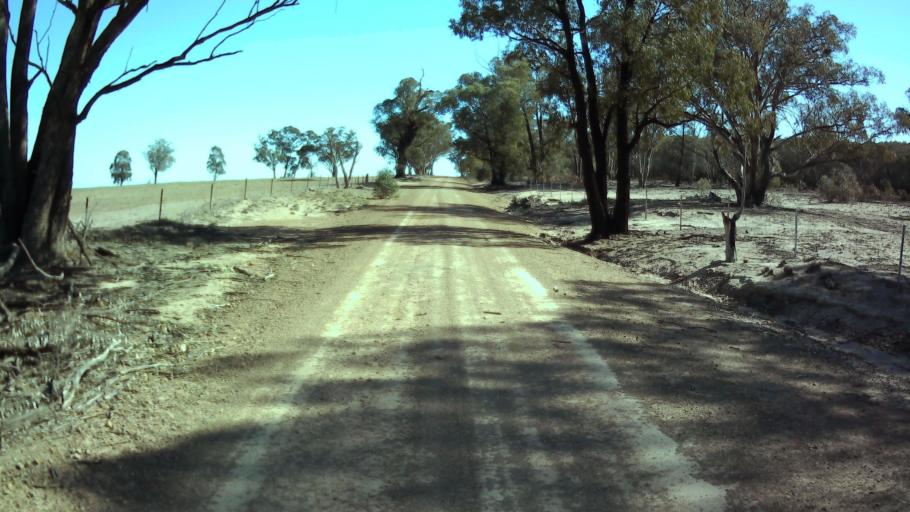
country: AU
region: New South Wales
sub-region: Weddin
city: Grenfell
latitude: -33.7563
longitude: 147.9198
